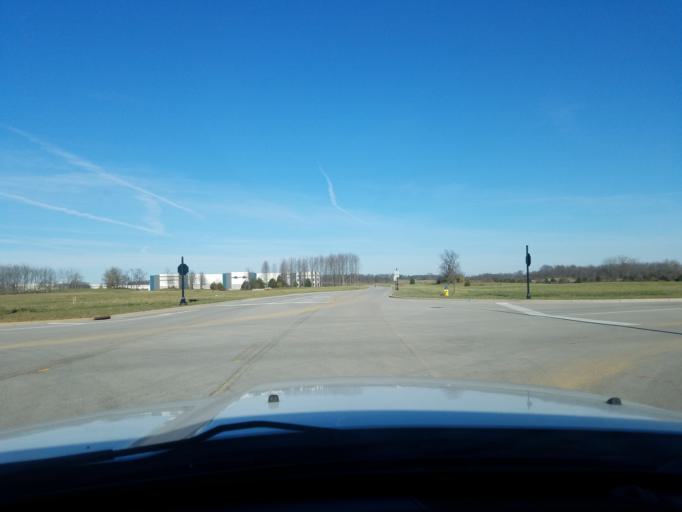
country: US
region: Indiana
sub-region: Clark County
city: Charlestown
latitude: 38.3806
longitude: -85.6814
